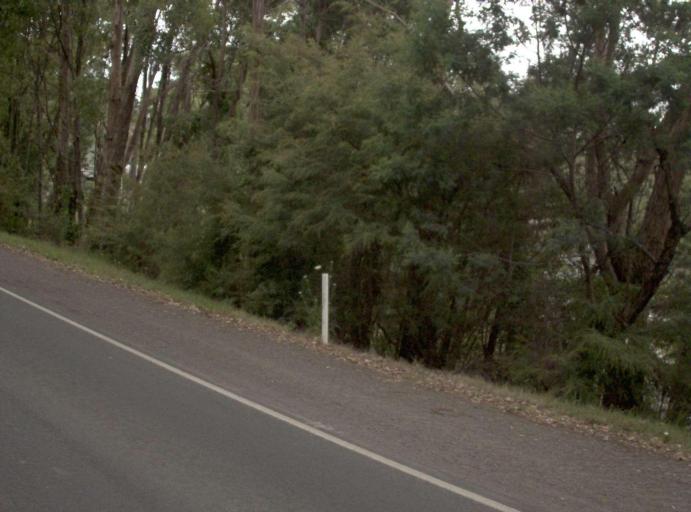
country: AU
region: Victoria
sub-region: Yarra Ranges
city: Launching Place
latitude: -37.7808
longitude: 145.5663
